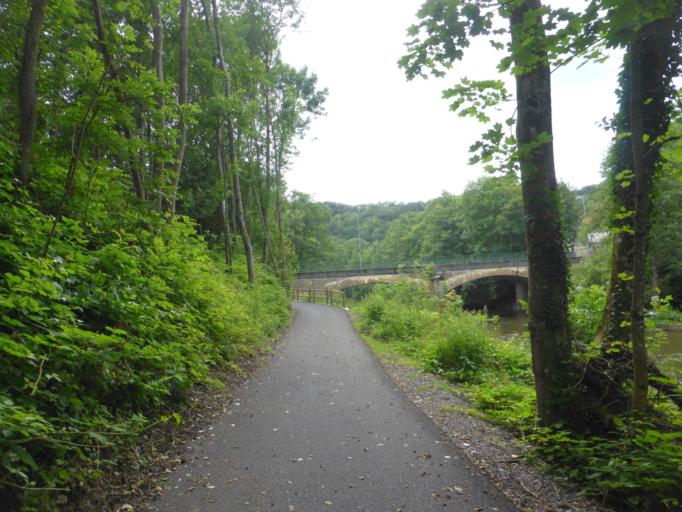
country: FR
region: Champagne-Ardenne
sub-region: Departement des Ardennes
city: Montherme
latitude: 49.8806
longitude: 4.7425
